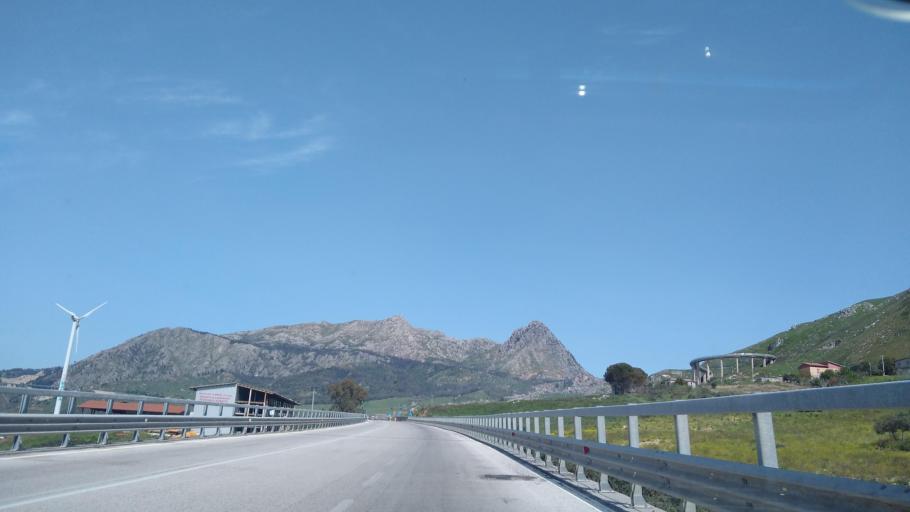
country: IT
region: Sicily
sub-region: Palermo
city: San Giuseppe Jato
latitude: 37.9765
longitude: 13.2163
